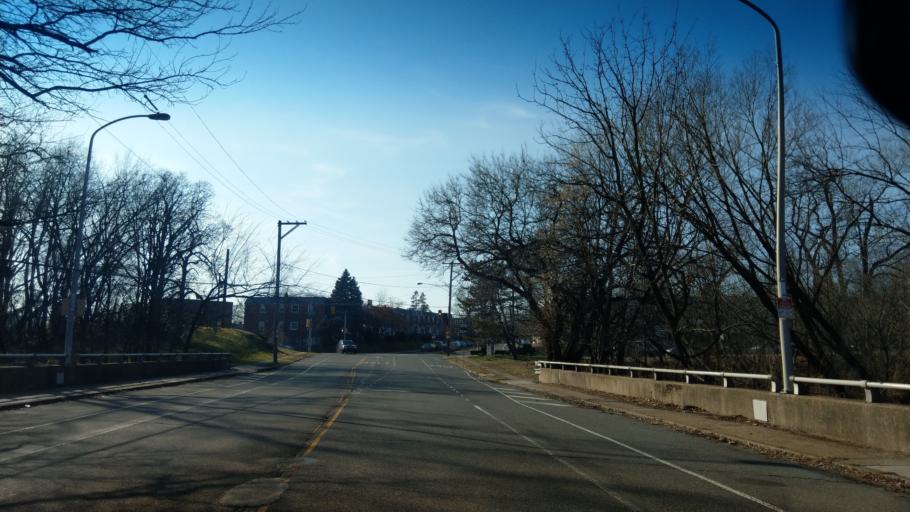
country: US
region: Pennsylvania
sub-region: Montgomery County
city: Rockledge
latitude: 40.0311
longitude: -75.1109
